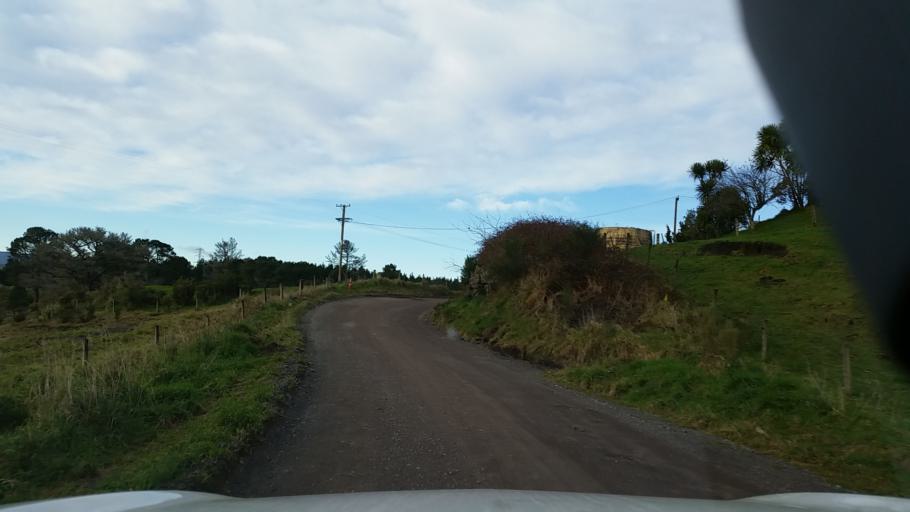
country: NZ
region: Bay of Plenty
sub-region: Rotorua District
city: Rotorua
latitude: -38.2290
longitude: 176.1600
